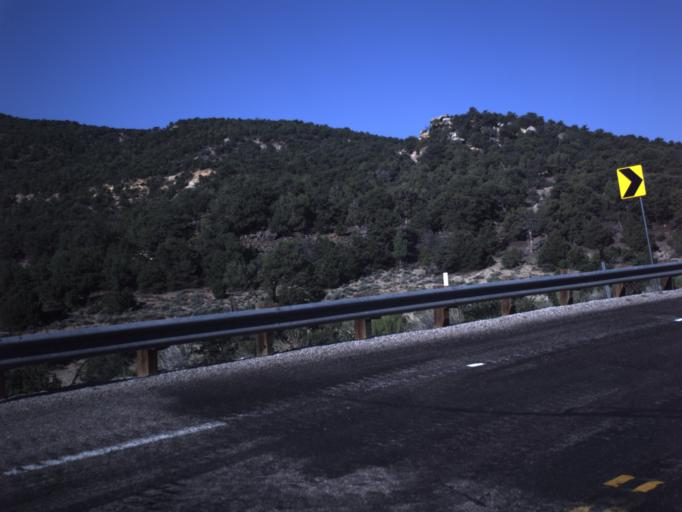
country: US
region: Utah
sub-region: Wayne County
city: Loa
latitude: 38.6718
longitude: -111.4065
